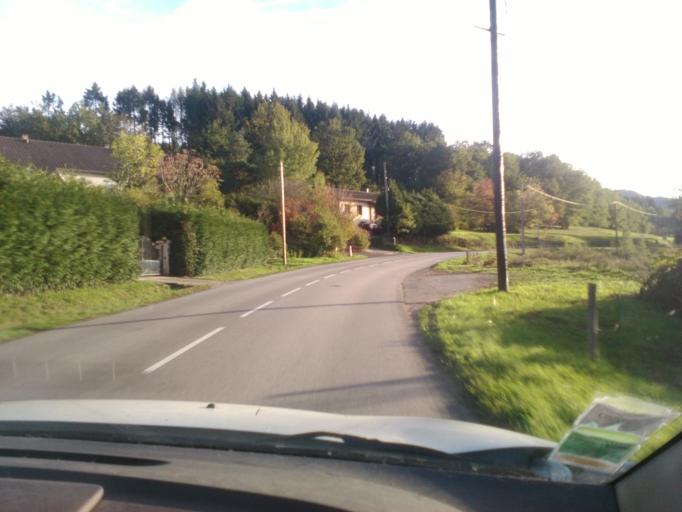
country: FR
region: Lorraine
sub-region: Departement des Vosges
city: Taintrux
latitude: 48.2465
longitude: 6.8979
